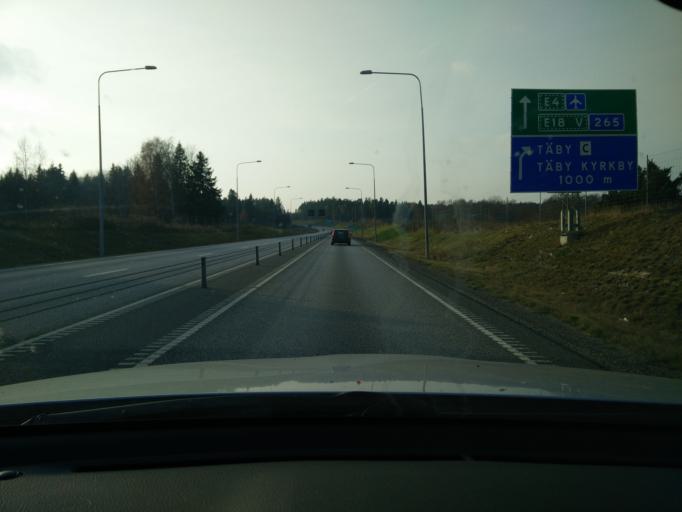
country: SE
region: Stockholm
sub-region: Taby Kommun
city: Taby
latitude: 59.4798
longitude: 18.0772
